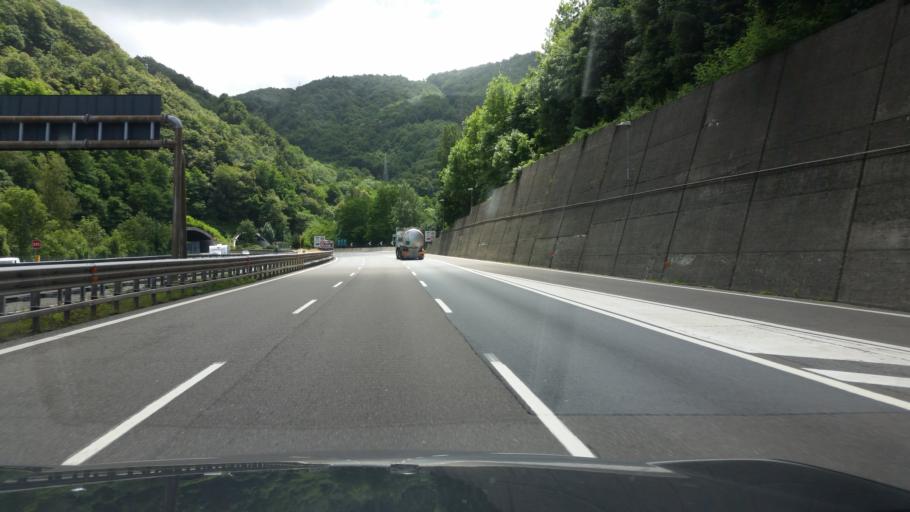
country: IT
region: Liguria
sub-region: Provincia di Genova
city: Masone
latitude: 44.5019
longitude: 8.7072
